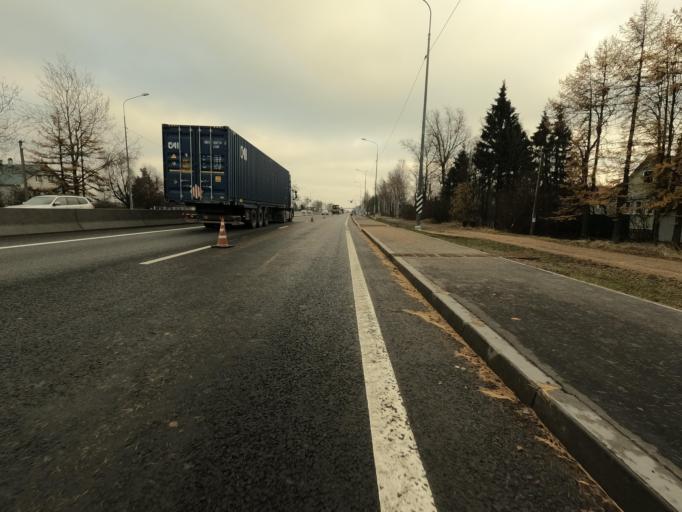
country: RU
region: Leningrad
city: Mga
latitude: 59.7236
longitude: 31.0959
